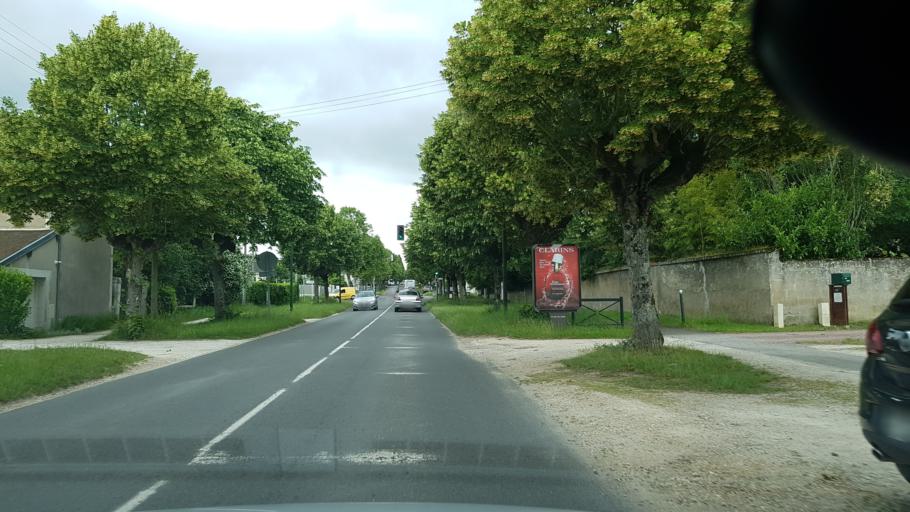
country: FR
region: Centre
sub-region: Departement d'Indre-et-Loire
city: Amboise
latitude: 47.4028
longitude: 0.9801
